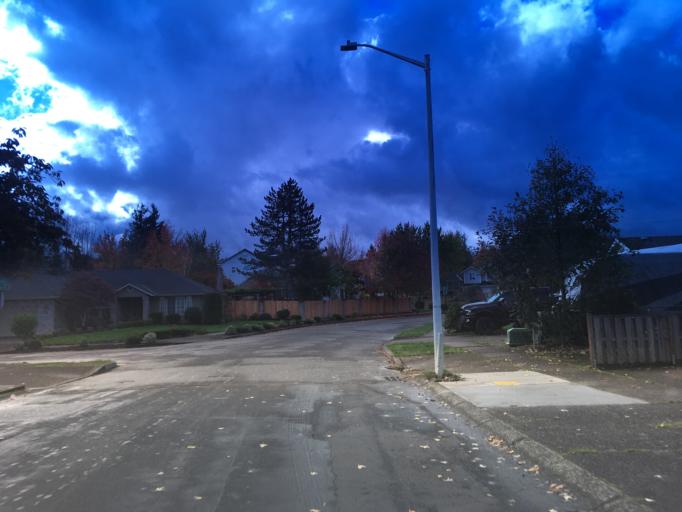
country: US
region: Oregon
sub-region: Multnomah County
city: Troutdale
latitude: 45.5120
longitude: -122.3798
